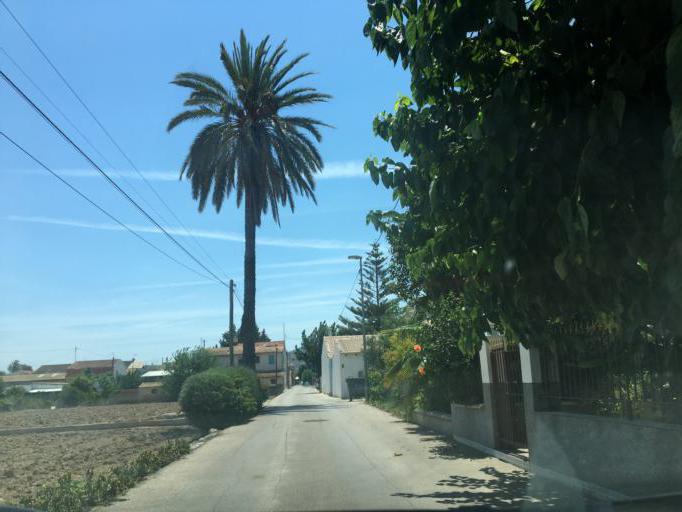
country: ES
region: Murcia
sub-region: Murcia
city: Santomera
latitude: 38.0184
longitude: -1.0556
